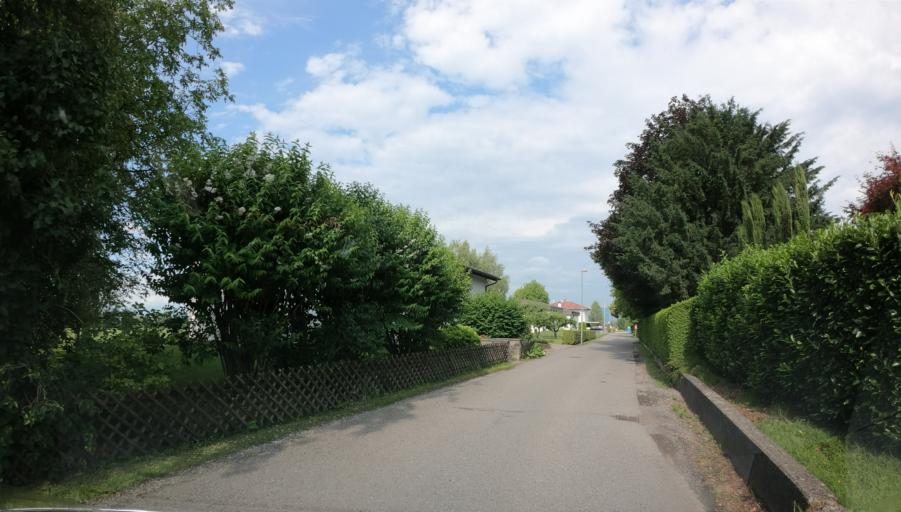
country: AT
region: Vorarlberg
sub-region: Politischer Bezirk Dornbirn
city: Dornbirn
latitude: 47.4058
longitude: 9.7180
